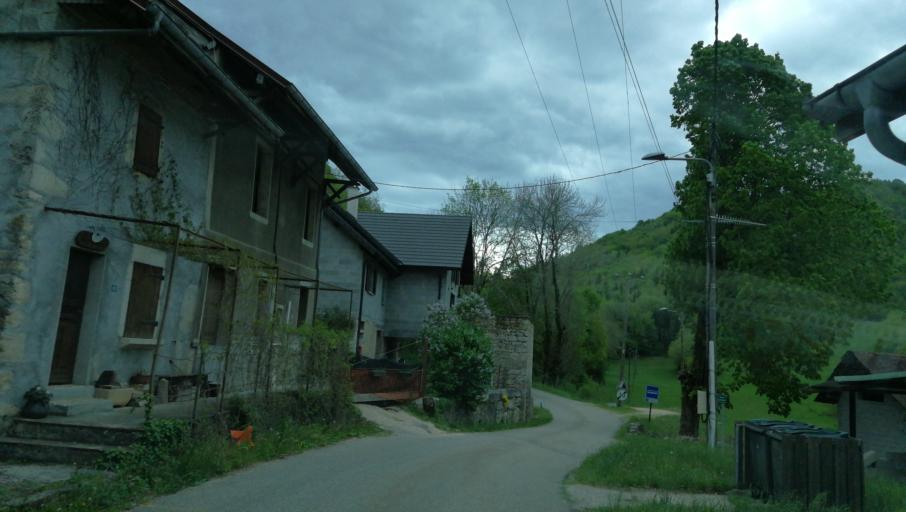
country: FR
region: Rhone-Alpes
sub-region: Departement de la Savoie
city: Chatillon
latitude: 45.7671
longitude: 5.8237
